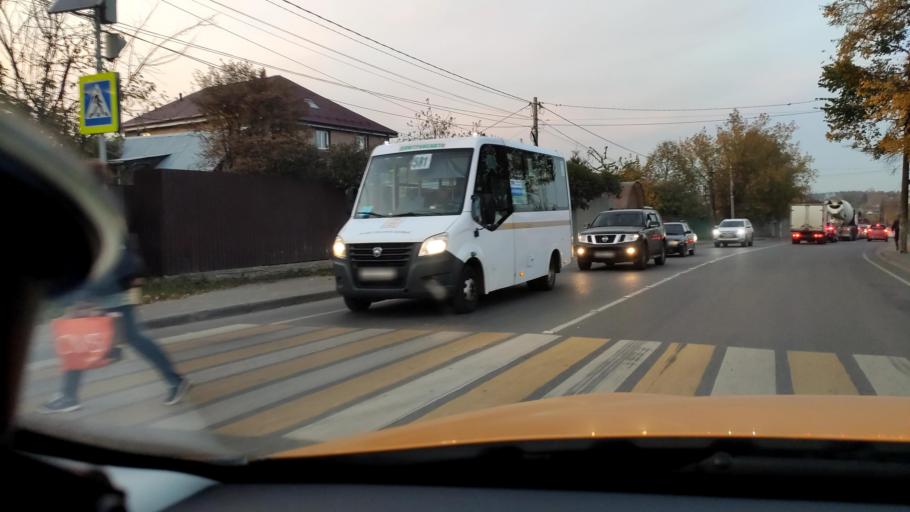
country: RU
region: Moskovskaya
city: Pirogovskiy
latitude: 55.9734
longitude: 37.7218
